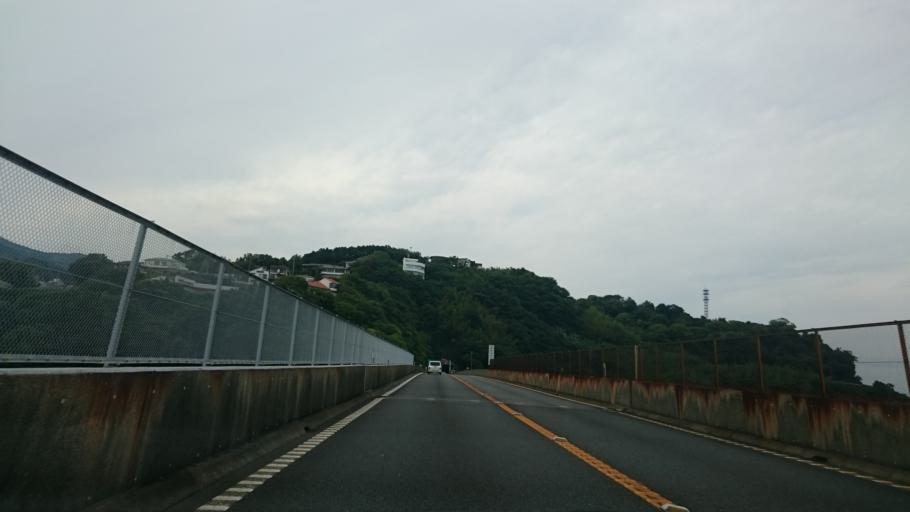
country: JP
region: Kanagawa
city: Yugawara
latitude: 35.1615
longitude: 139.1432
